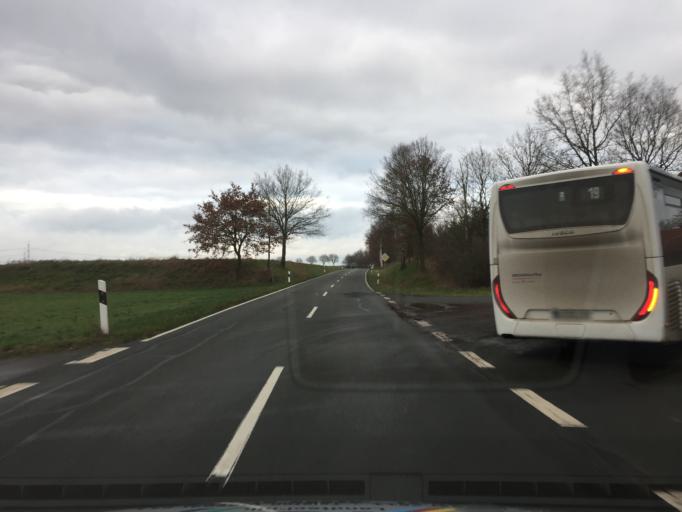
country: DE
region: Lower Saxony
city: Steyerberg
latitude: 52.5342
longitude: 9.0274
